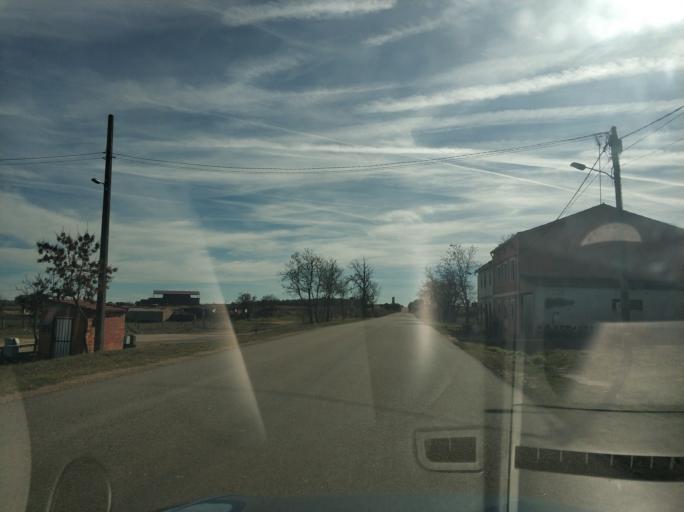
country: ES
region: Castille and Leon
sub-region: Provincia de Zamora
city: Cuelgamures
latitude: 41.2530
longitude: -5.7093
